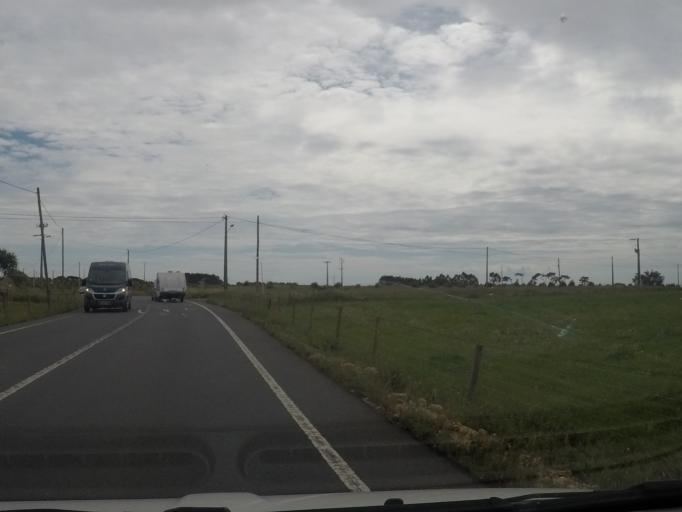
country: PT
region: Setubal
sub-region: Sines
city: Porto Covo
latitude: 37.8782
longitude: -8.7599
